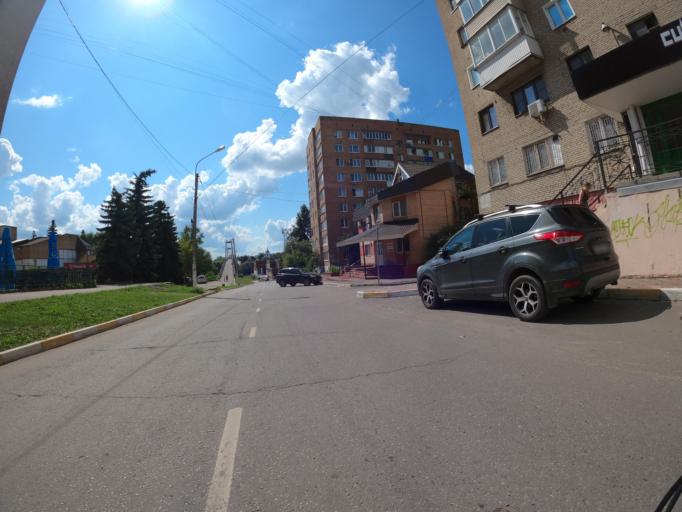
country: RU
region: Moskovskaya
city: Voskresensk
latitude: 55.3205
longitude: 38.6676
